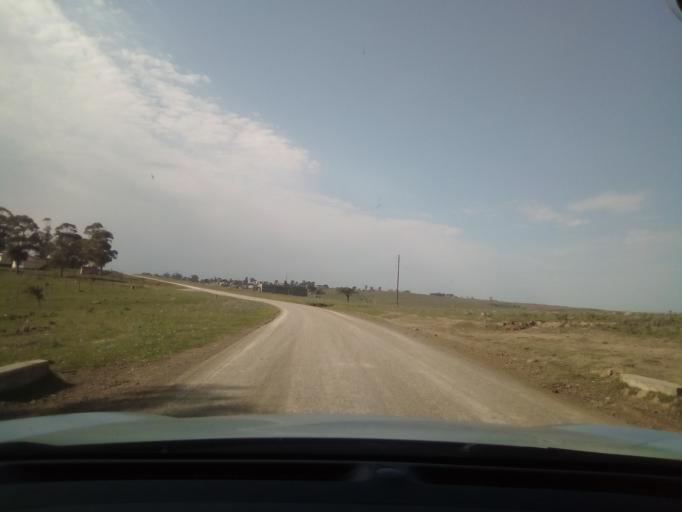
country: ZA
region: Eastern Cape
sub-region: Buffalo City Metropolitan Municipality
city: Bhisho
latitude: -32.9870
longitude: 27.2555
